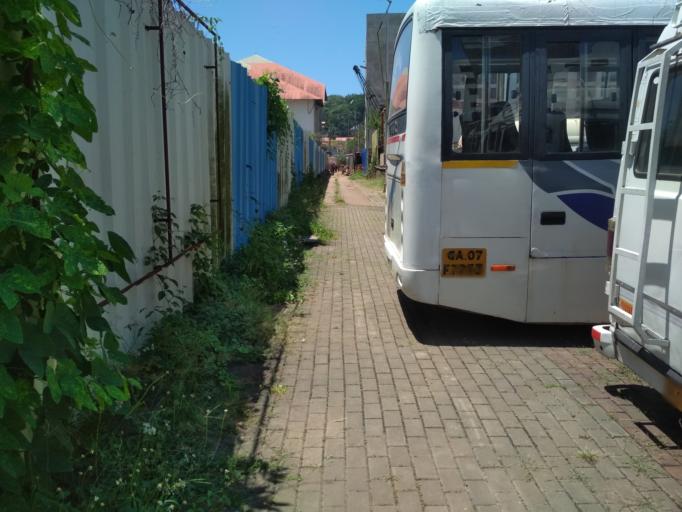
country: IN
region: Goa
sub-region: North Goa
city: Panaji
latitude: 15.4943
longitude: 73.8346
